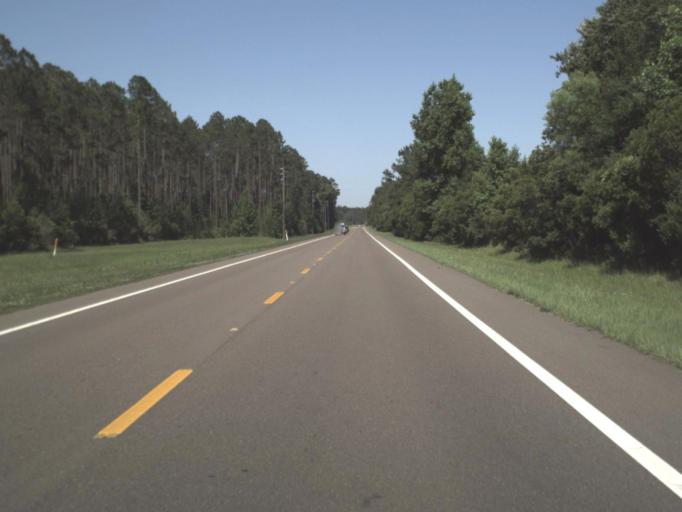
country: US
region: Florida
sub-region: Duval County
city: Baldwin
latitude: 30.2986
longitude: -82.0350
